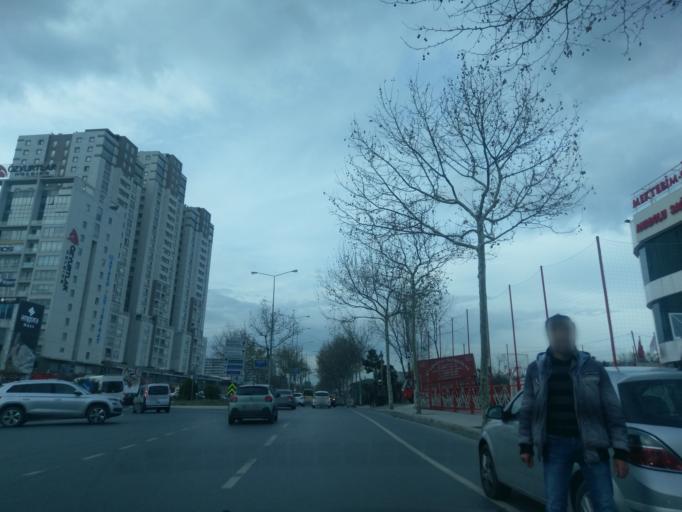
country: TR
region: Istanbul
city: Esenyurt
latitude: 41.0648
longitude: 28.6725
